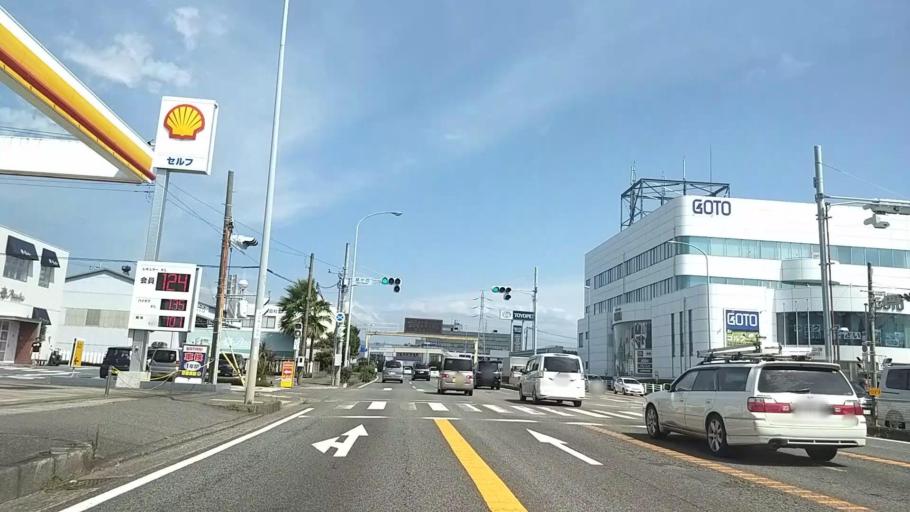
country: JP
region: Shizuoka
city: Numazu
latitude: 35.1208
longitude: 138.8736
